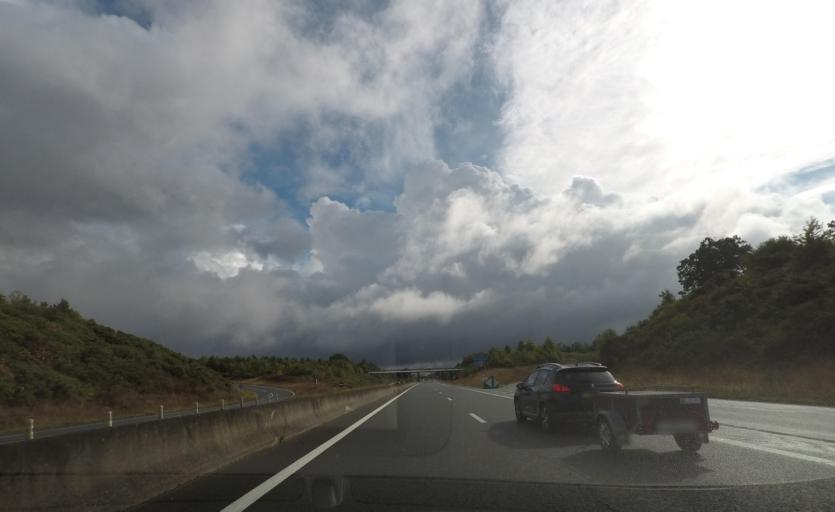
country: FR
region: Pays de la Loire
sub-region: Departement de la Vendee
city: La Ferriere
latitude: 46.6692
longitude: -1.3556
